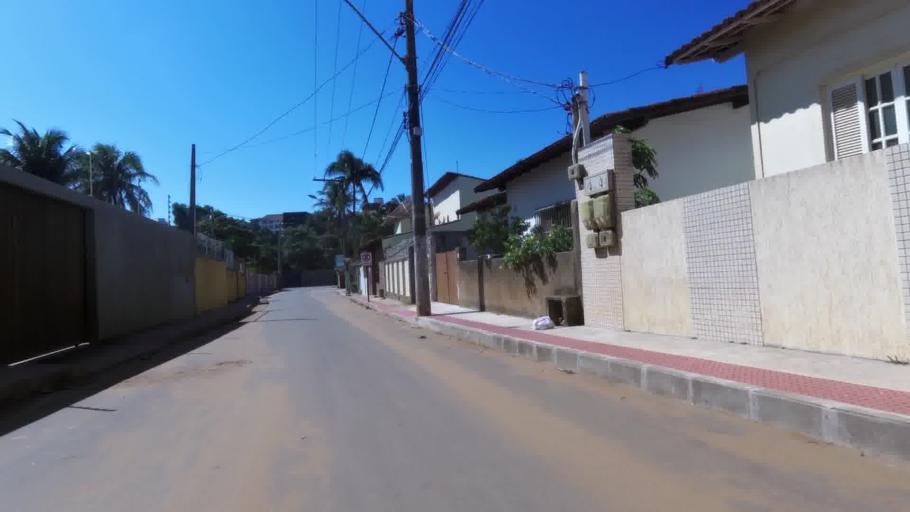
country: BR
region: Espirito Santo
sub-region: Guarapari
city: Guarapari
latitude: -20.7385
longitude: -40.5375
